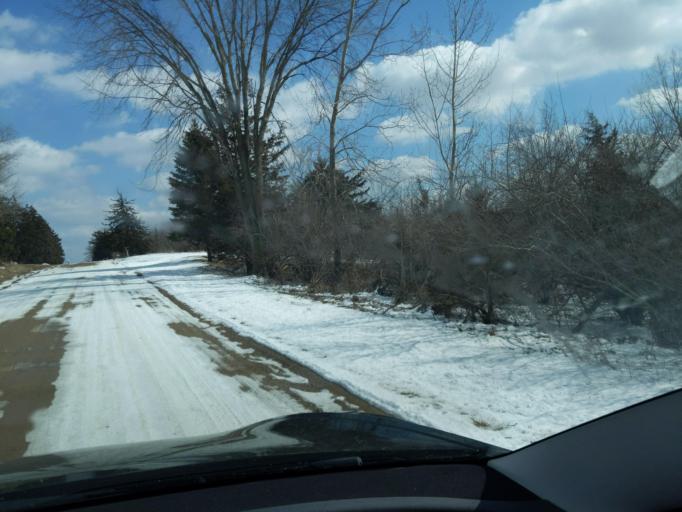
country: US
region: Michigan
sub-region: Livingston County
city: Fowlerville
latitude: 42.6139
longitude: -84.0660
